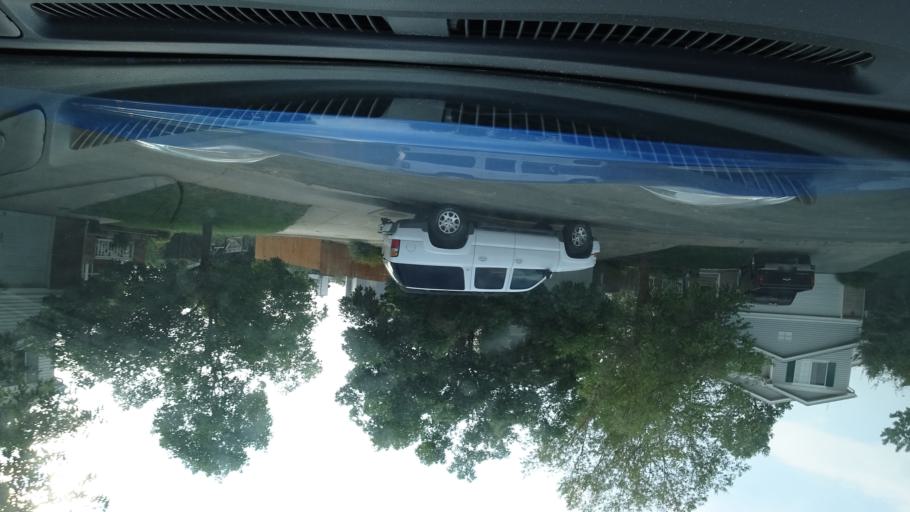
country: US
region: Colorado
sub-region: Adams County
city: Aurora
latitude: 39.7463
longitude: -104.7606
